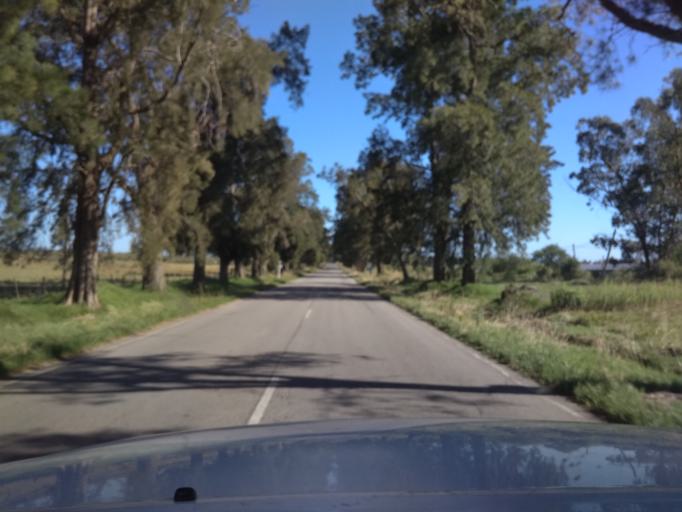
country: UY
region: Canelones
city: San Bautista
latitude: -34.3890
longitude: -55.9596
